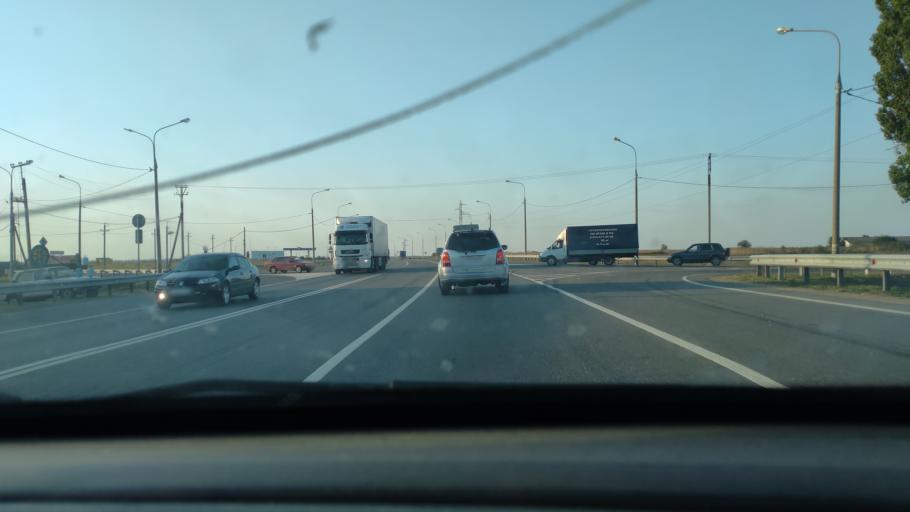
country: RU
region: Krasnodarskiy
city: Kanevskaya
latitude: 46.0764
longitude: 39.0145
